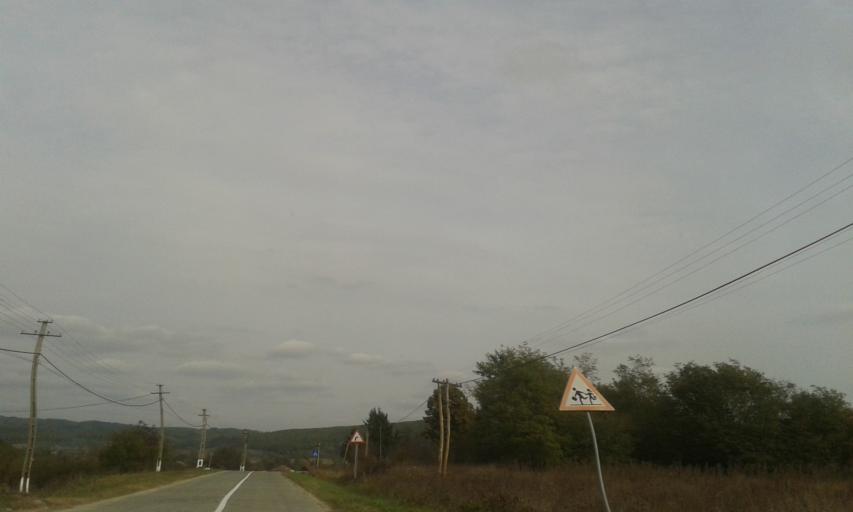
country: RO
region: Valcea
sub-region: Comuna Gradistea
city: Gradistea
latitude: 44.9000
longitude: 23.8171
